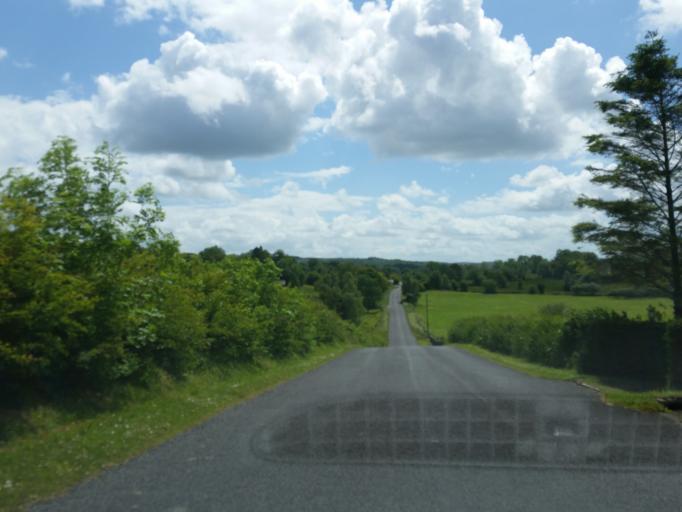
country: GB
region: Northern Ireland
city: Fivemiletown
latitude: 54.3460
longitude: -7.2965
